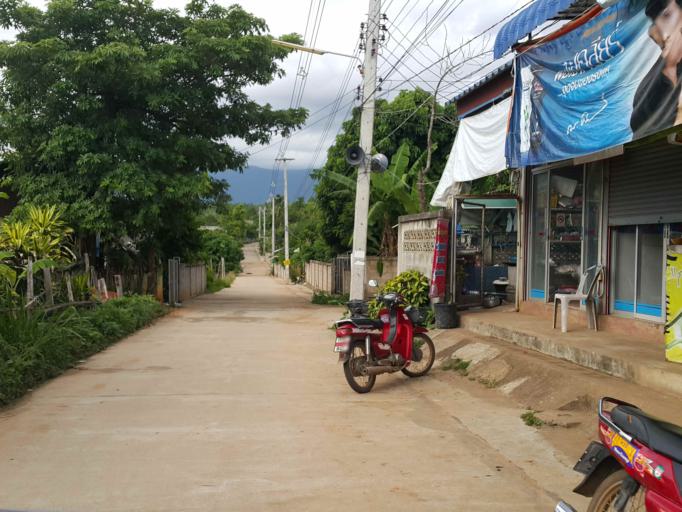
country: TH
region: Chiang Mai
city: Mae Chaem
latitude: 18.4885
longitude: 98.3779
